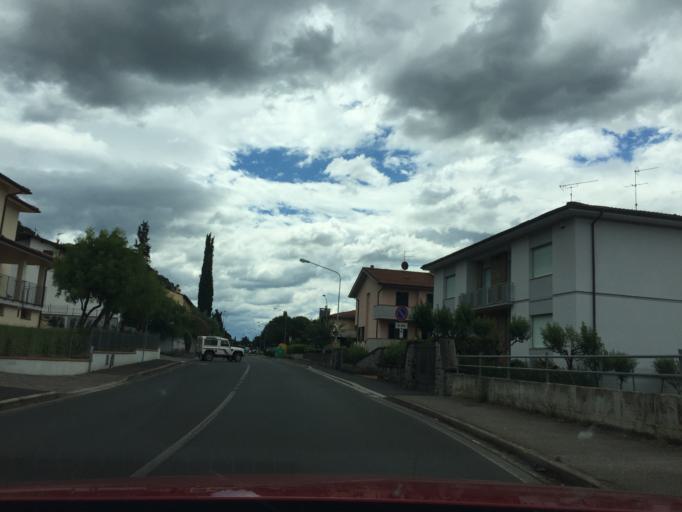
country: IT
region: Tuscany
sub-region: Province of Florence
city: Montelupo Fiorentino
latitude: 43.7290
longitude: 11.0262
